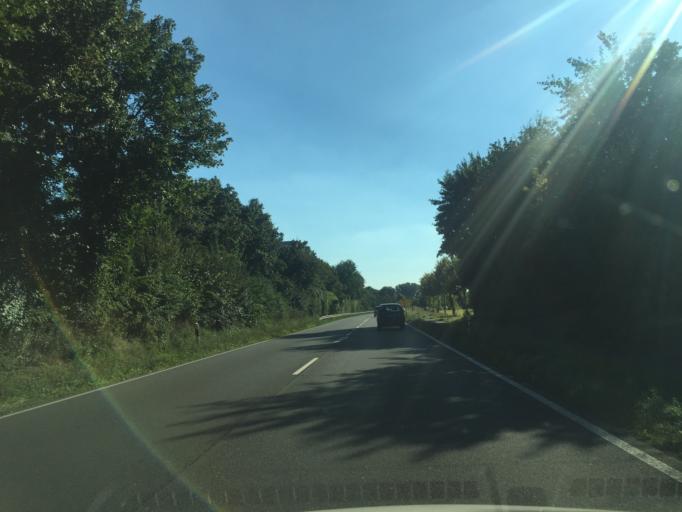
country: DE
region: North Rhine-Westphalia
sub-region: Regierungsbezirk Munster
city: Telgte
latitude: 51.9845
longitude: 7.7737
